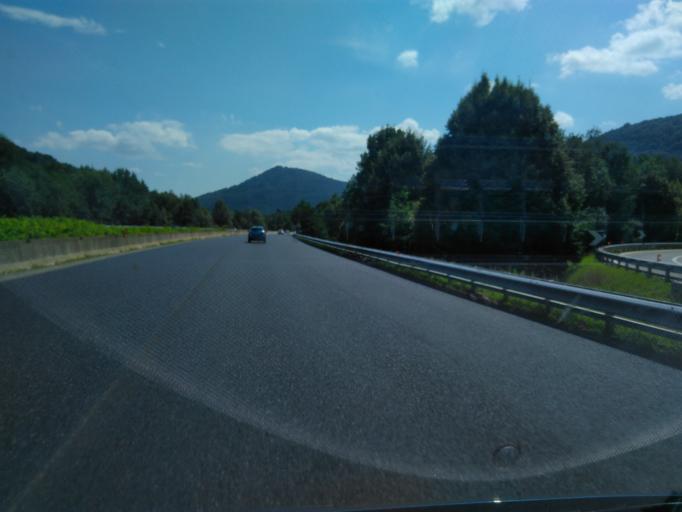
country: IT
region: Piedmont
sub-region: Provincia Verbano-Cusio-Ossola
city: Stresa
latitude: 45.8613
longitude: 8.5401
